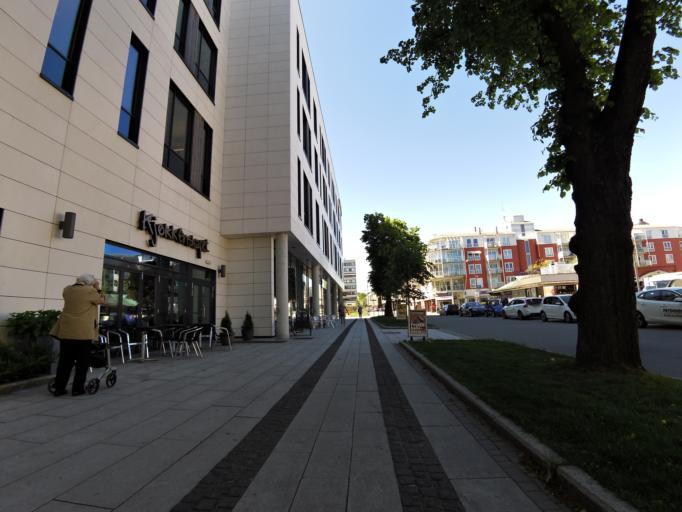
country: NO
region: Vest-Agder
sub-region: Kristiansand
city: Kristiansand
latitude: 58.1474
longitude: 8.0066
